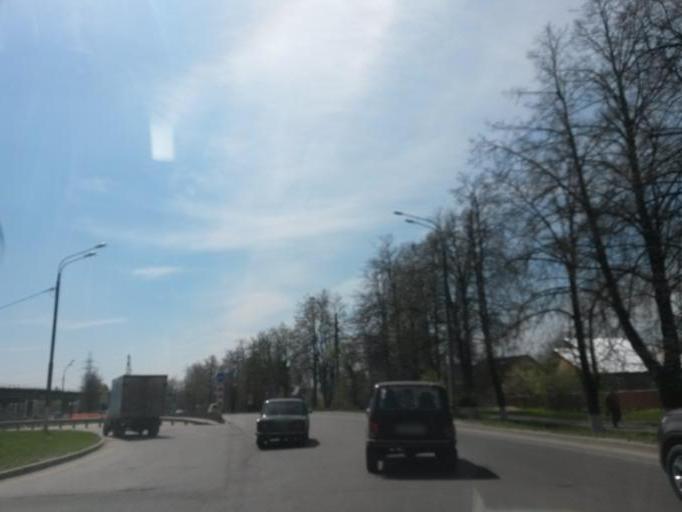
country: RU
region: Moskovskaya
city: Klimovsk
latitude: 55.3862
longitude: 37.5383
